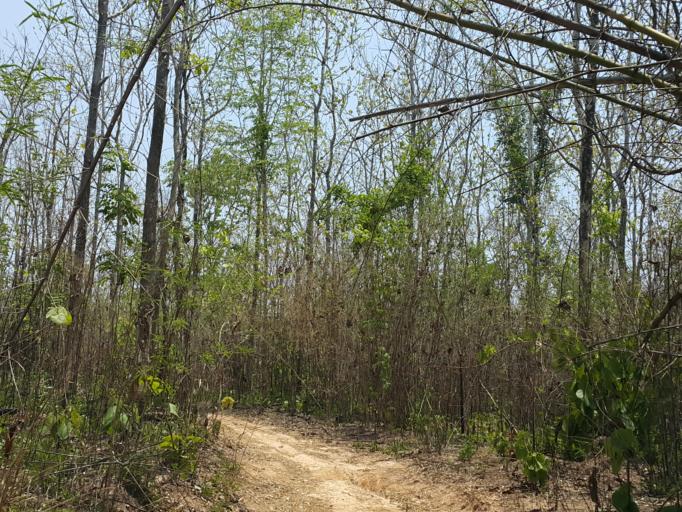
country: TH
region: Kanchanaburi
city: Sai Yok
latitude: 14.2278
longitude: 98.8826
